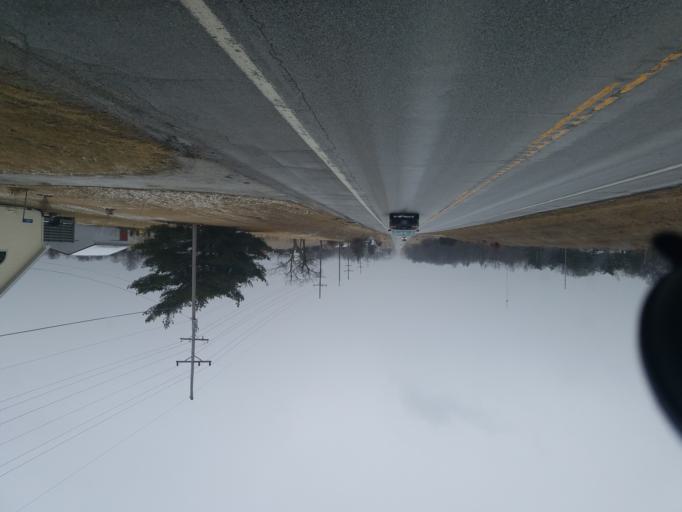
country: US
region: Missouri
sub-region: Adair County
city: Kirksville
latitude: 40.2738
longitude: -92.5825
